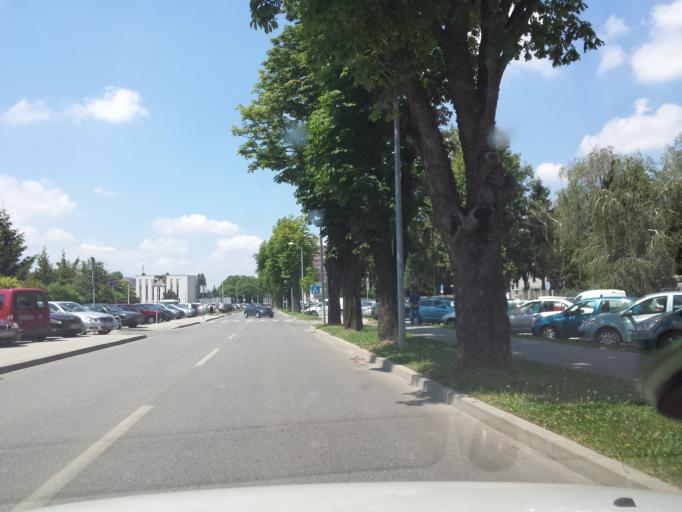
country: HR
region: Grad Zagreb
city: Jankomir
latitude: 45.8008
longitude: 15.9340
